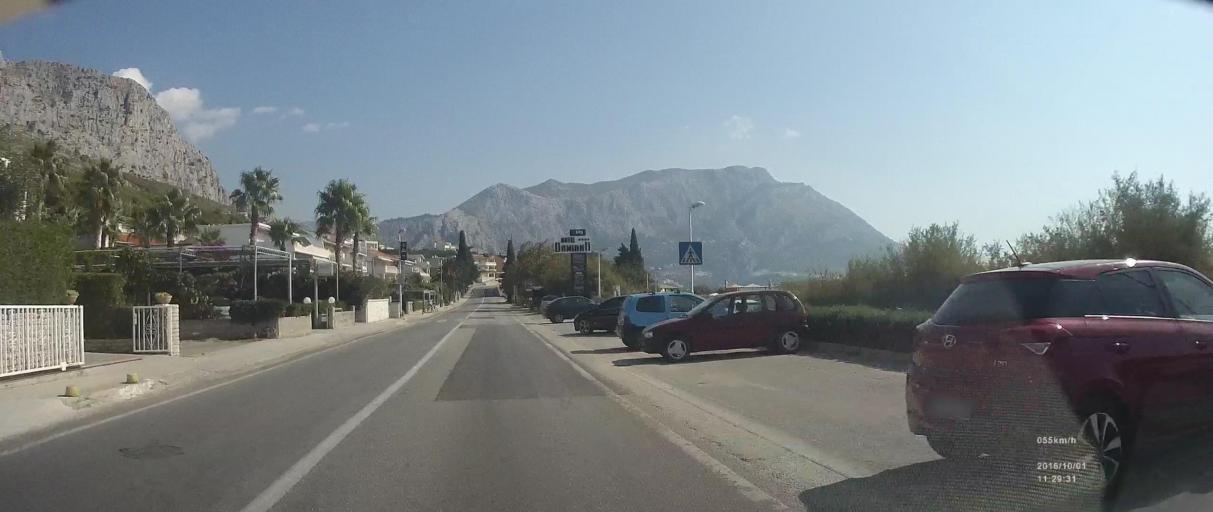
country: HR
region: Splitsko-Dalmatinska
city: Duce
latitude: 43.4395
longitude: 16.6672
